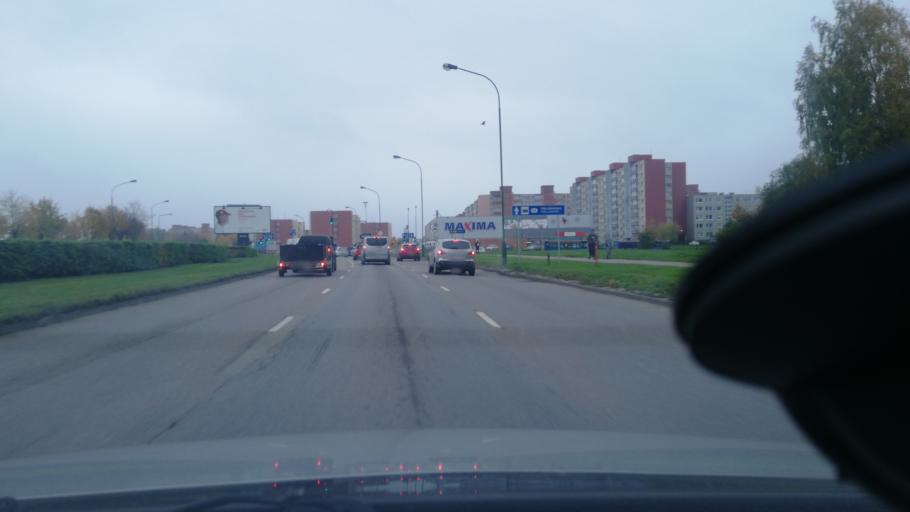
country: LT
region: Klaipedos apskritis
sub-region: Klaipeda
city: Klaipeda
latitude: 55.6787
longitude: 21.1879
